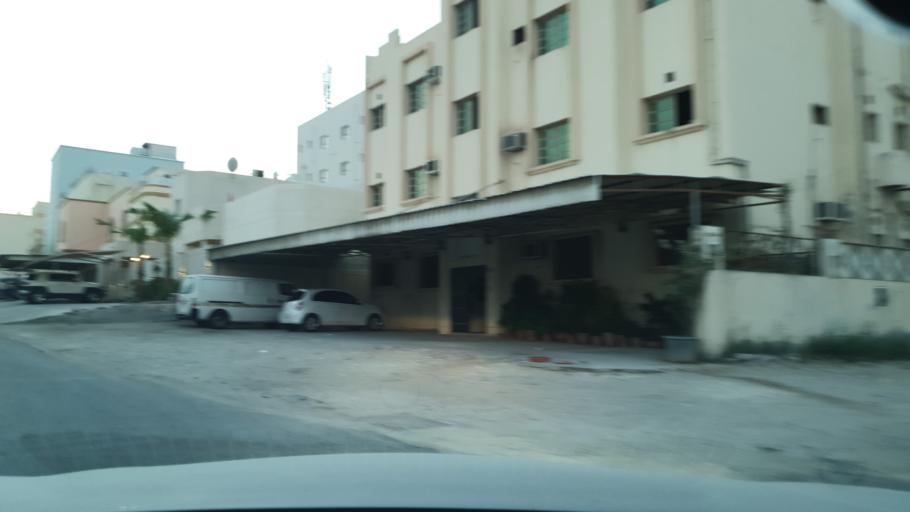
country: BH
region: Northern
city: Ar Rifa'
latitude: 26.1215
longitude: 50.5856
